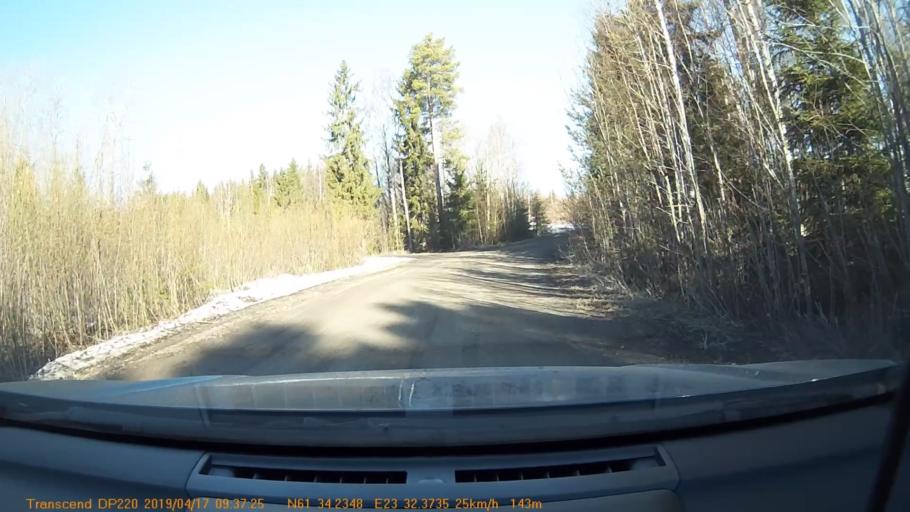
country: FI
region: Pirkanmaa
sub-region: Tampere
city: Yloejaervi
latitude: 61.5706
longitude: 23.5396
